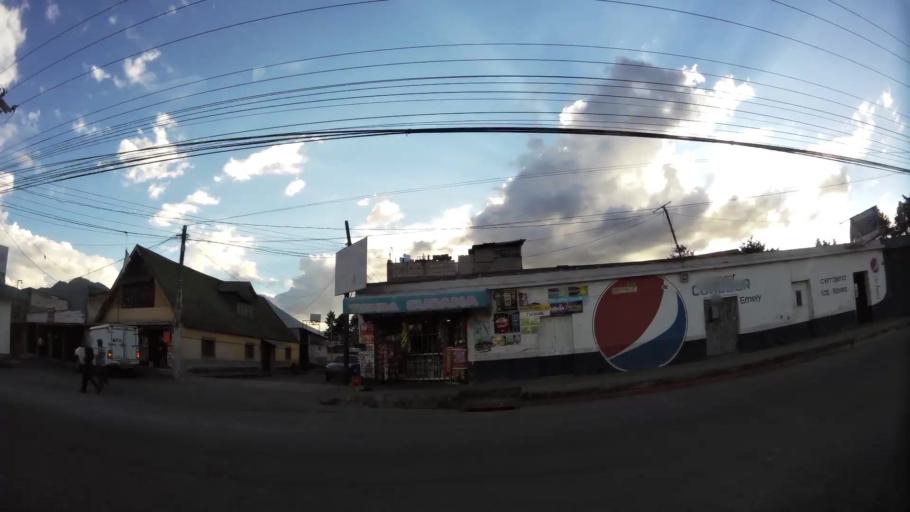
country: GT
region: Quetzaltenango
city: Quetzaltenango
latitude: 14.8501
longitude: -91.5295
